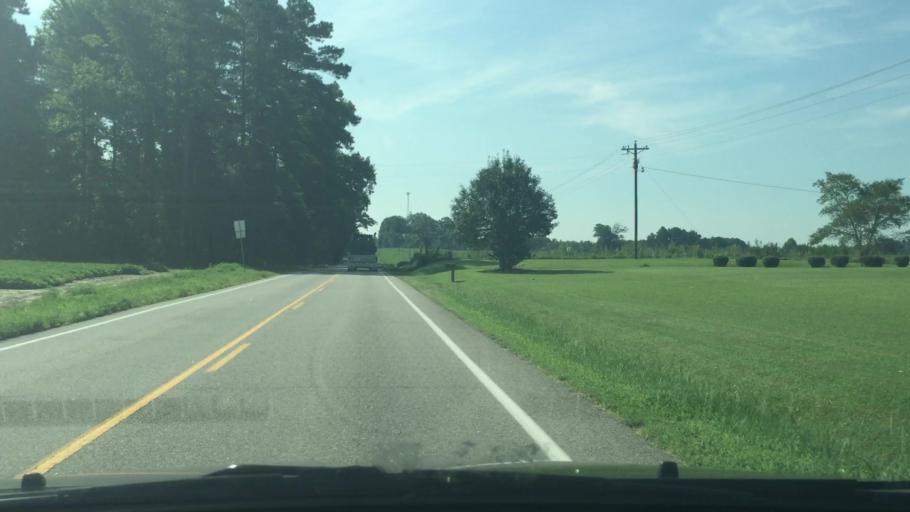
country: US
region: Virginia
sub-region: Sussex County
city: Sussex
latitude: 37.0430
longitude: -77.3117
